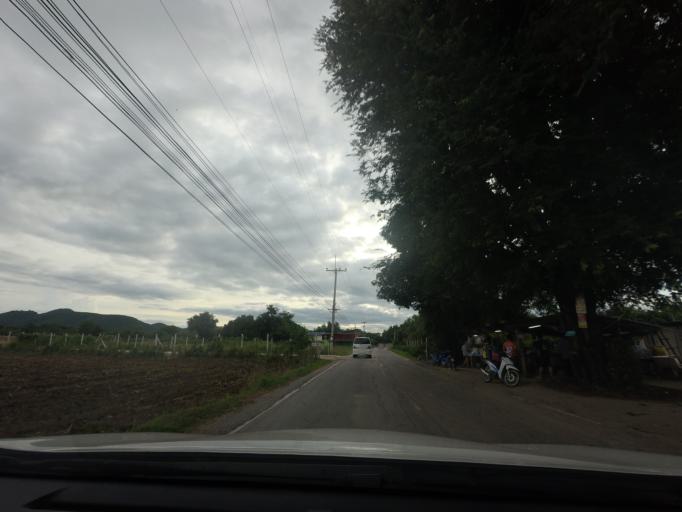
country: TH
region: Nakhon Ratchasima
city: Pak Chong
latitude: 14.6069
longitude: 101.4386
